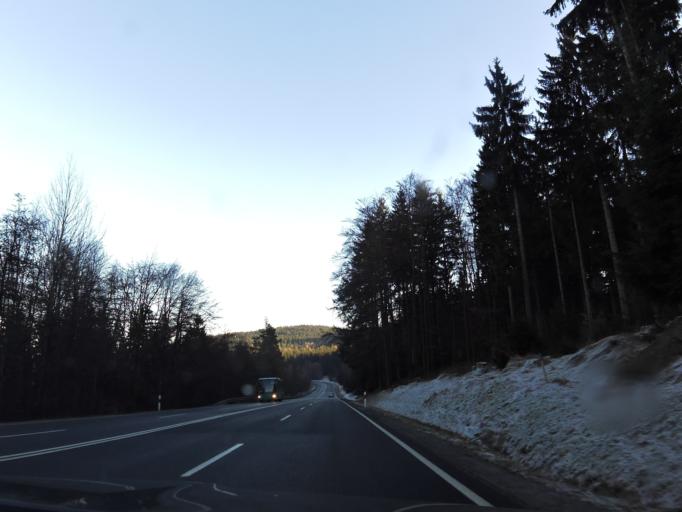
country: DE
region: Bavaria
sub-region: Upper Franconia
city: Nagel
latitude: 50.0041
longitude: 11.9094
